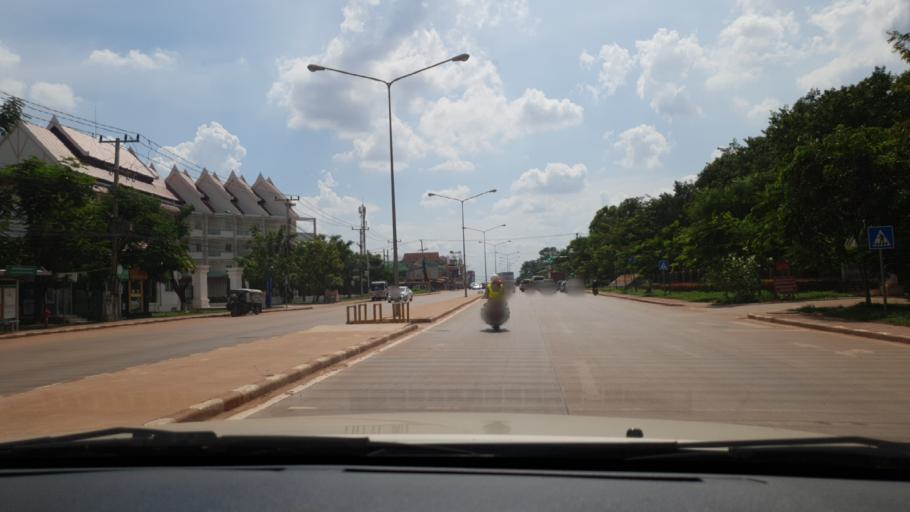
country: LA
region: Vientiane
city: Vientiane
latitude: 18.0337
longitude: 102.6360
